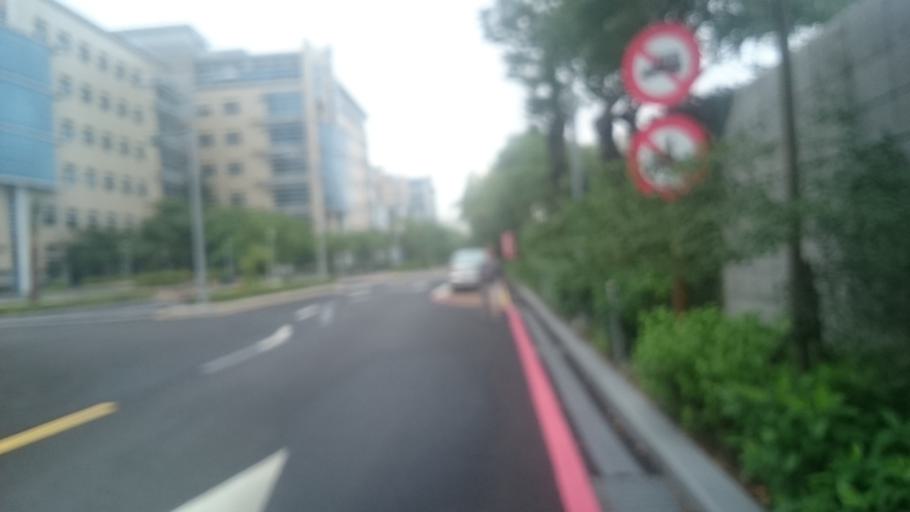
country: TW
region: Taiwan
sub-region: Hsinchu
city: Zhubei
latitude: 24.8394
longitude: 121.0122
